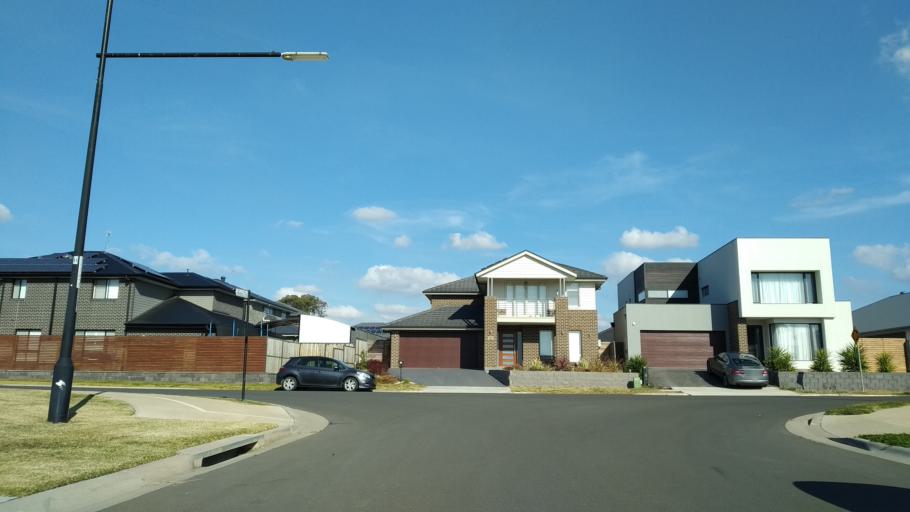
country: AU
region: New South Wales
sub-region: Blacktown
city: Hassall Grove
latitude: -33.7198
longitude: 150.8538
